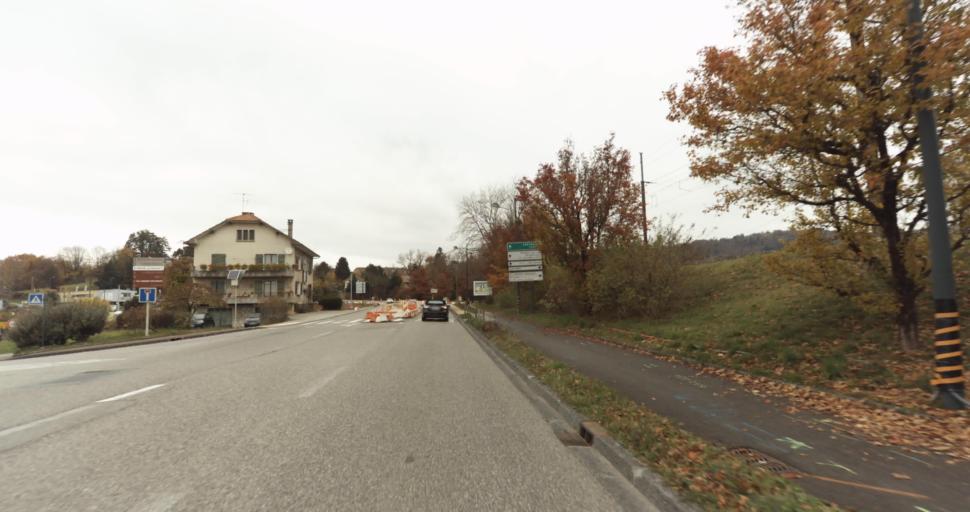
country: FR
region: Rhone-Alpes
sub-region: Departement de la Haute-Savoie
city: Pringy
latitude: 45.9420
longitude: 6.1231
